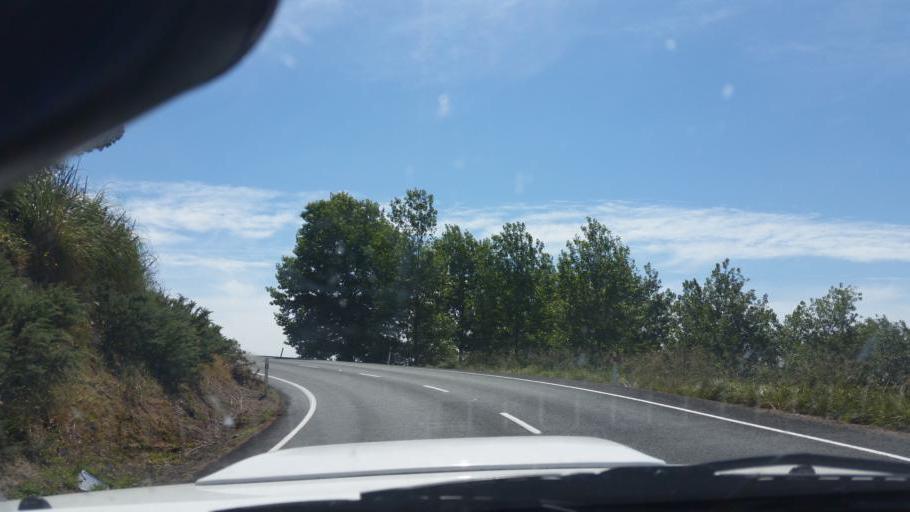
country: NZ
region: Auckland
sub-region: Auckland
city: Wellsford
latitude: -36.2239
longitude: 174.3773
